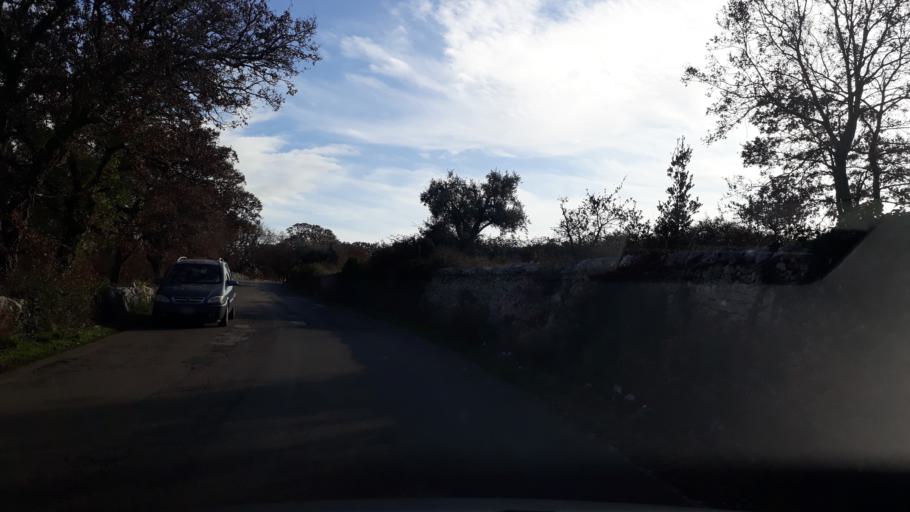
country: IT
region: Apulia
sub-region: Provincia di Taranto
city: Martina Franca
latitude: 40.6766
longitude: 17.3592
